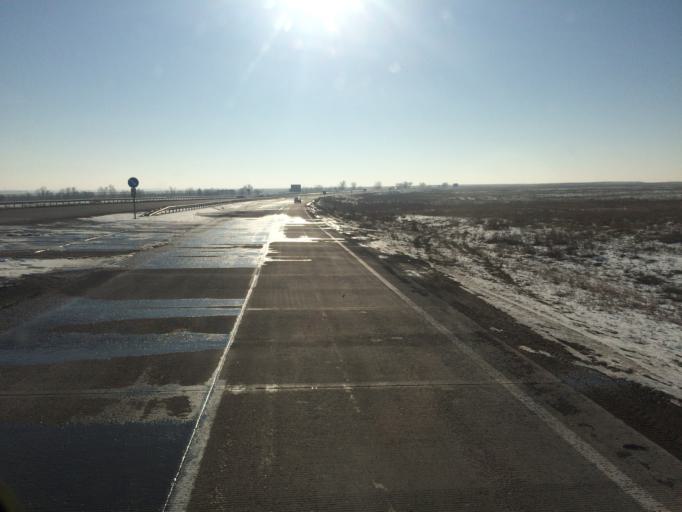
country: KG
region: Chuy
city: Kara-Balta
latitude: 43.1862
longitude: 73.9412
